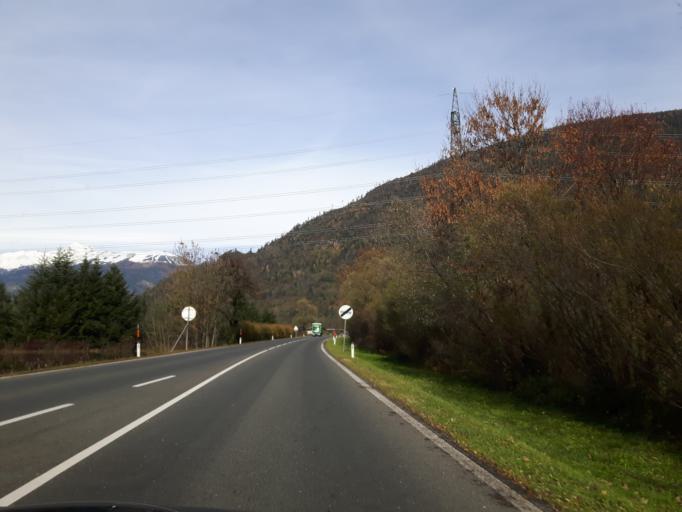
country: AT
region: Tyrol
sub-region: Politischer Bezirk Lienz
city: Nikolsdorf
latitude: 46.7916
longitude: 12.8759
